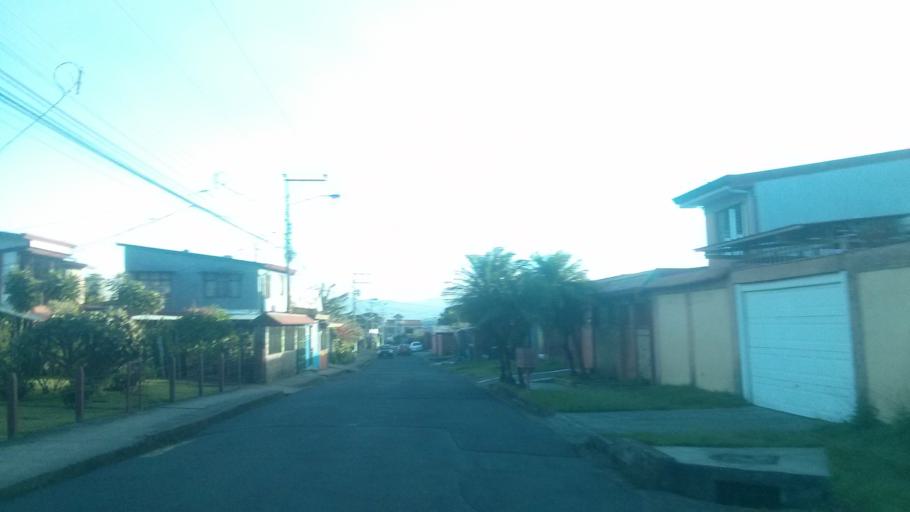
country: CR
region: Heredia
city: San Pablo
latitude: 9.9975
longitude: -84.0924
